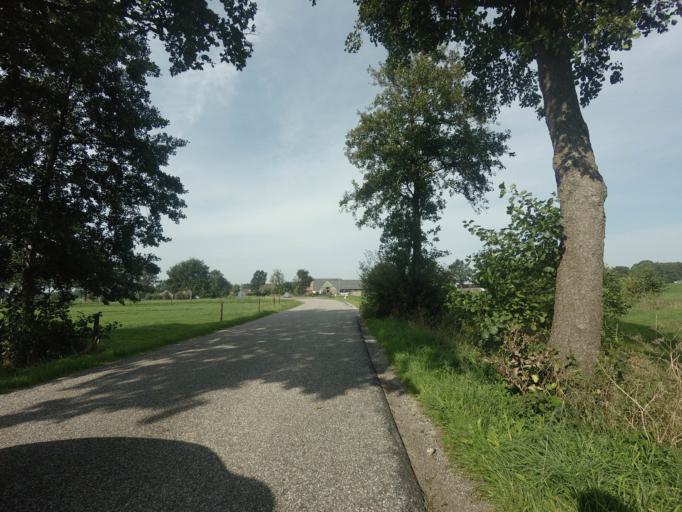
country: NL
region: Groningen
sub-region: Gemeente Leek
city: Leek
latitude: 53.1904
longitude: 6.3572
